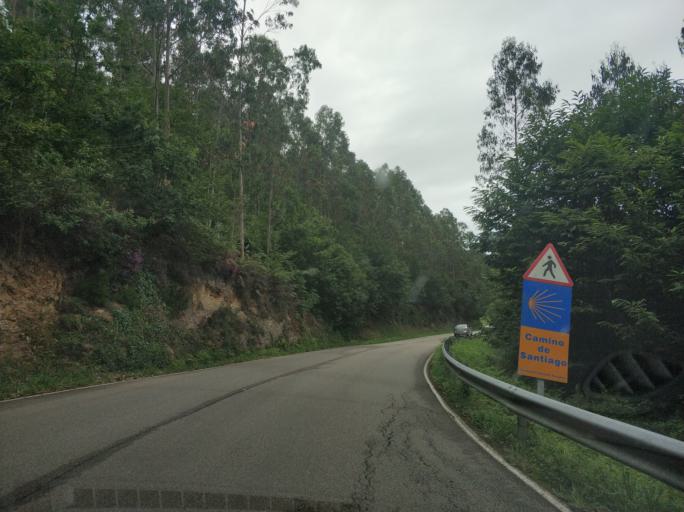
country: ES
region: Asturias
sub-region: Province of Asturias
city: Cudillero
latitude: 43.5635
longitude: -6.2405
